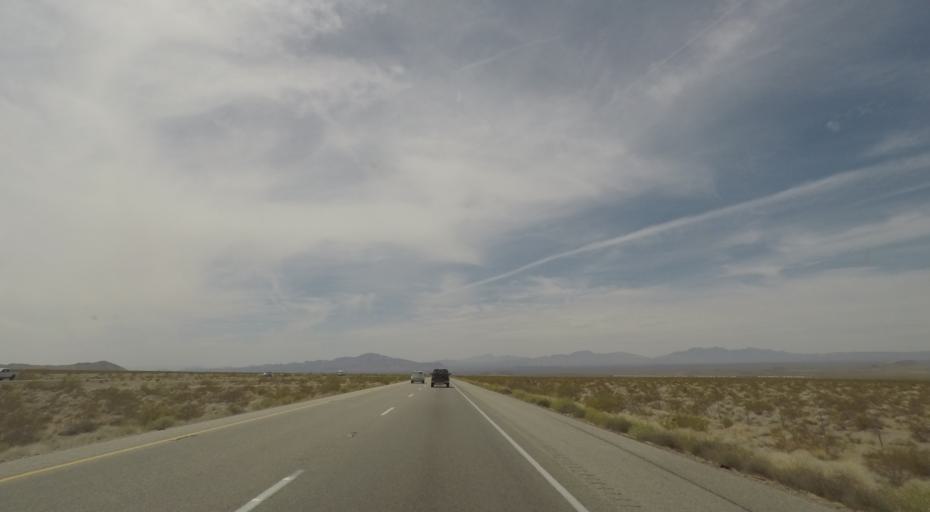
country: US
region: California
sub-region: San Bernardino County
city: Needles
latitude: 34.8235
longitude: -115.1020
